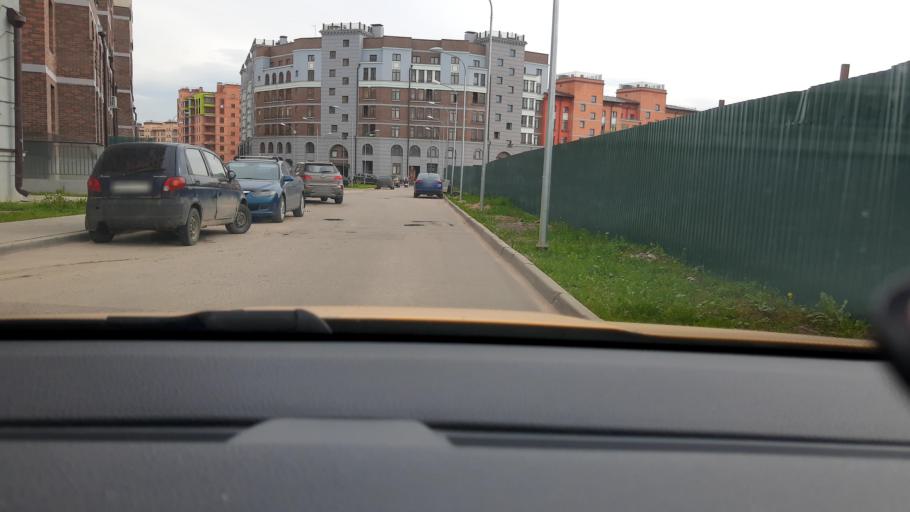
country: RU
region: Moskovskaya
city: Opalikha
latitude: 55.8811
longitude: 37.2689
